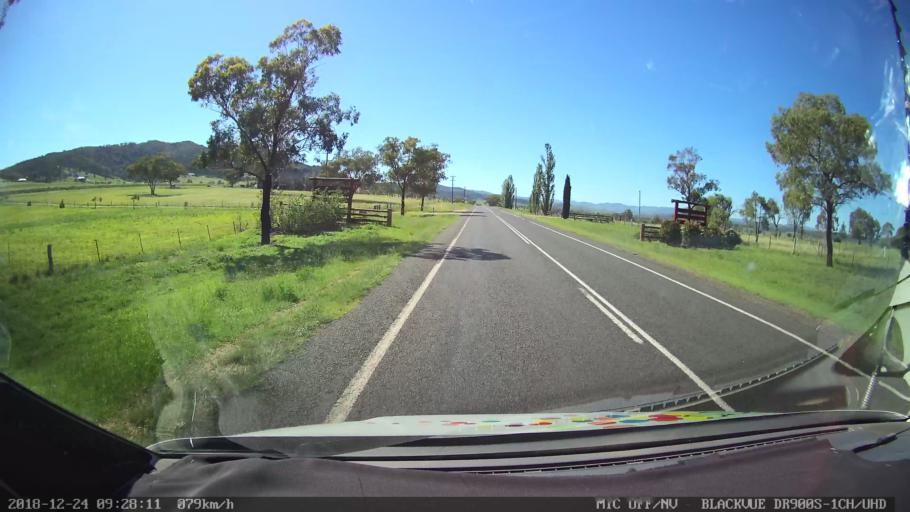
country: AU
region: New South Wales
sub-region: Liverpool Plains
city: Quirindi
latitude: -31.5353
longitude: 150.6867
